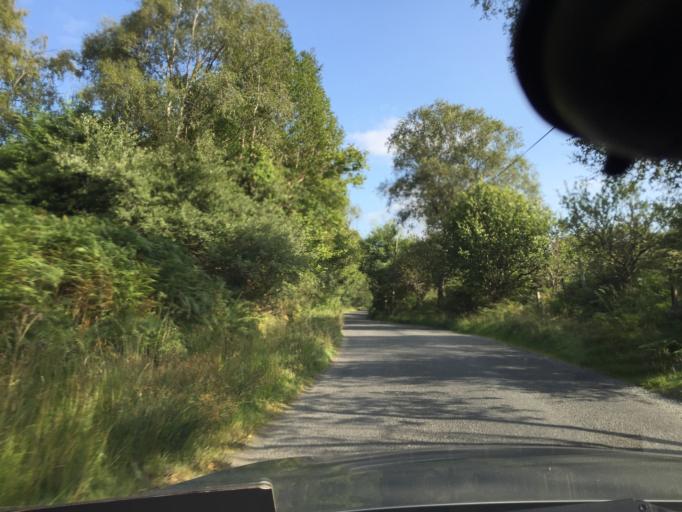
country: IE
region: Leinster
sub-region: Wicklow
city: Rathdrum
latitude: 53.0339
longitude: -6.3173
